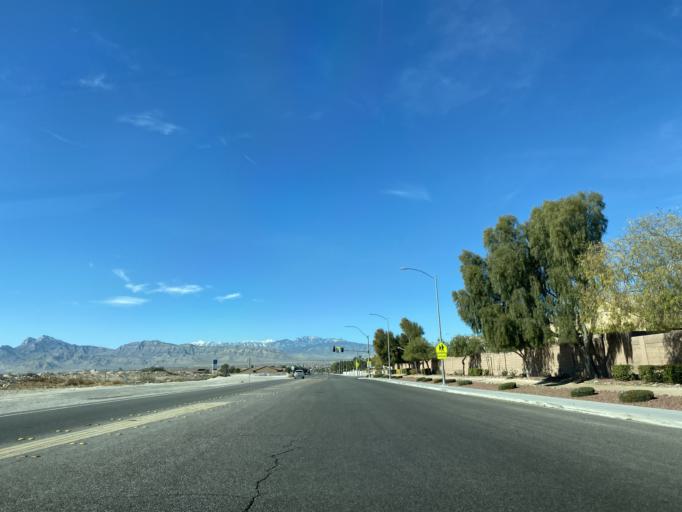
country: US
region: Nevada
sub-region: Clark County
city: North Las Vegas
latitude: 36.3051
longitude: -115.2314
